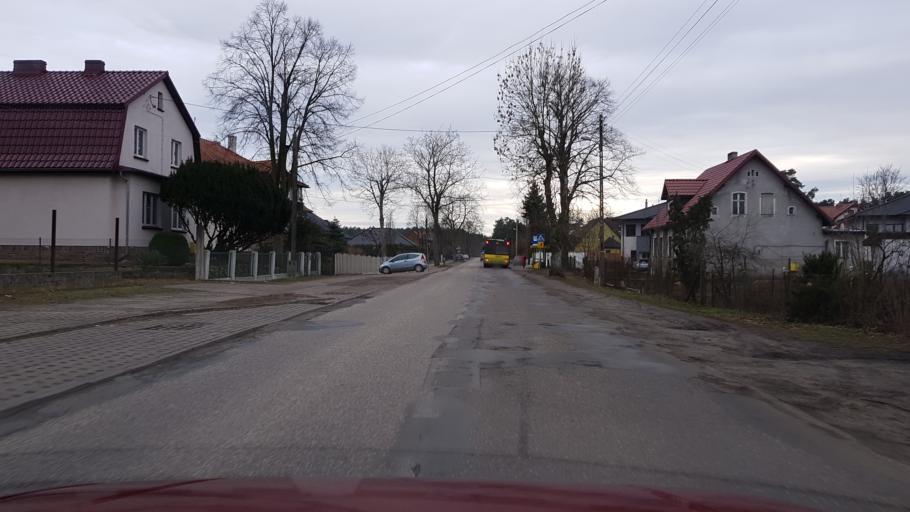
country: PL
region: West Pomeranian Voivodeship
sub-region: Powiat policki
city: Dobra
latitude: 53.5384
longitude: 14.4665
